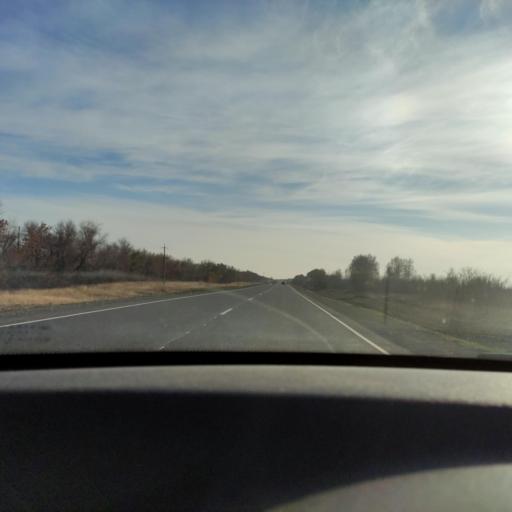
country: RU
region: Samara
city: Krasnoarmeyskoye
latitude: 52.8200
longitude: 50.0095
